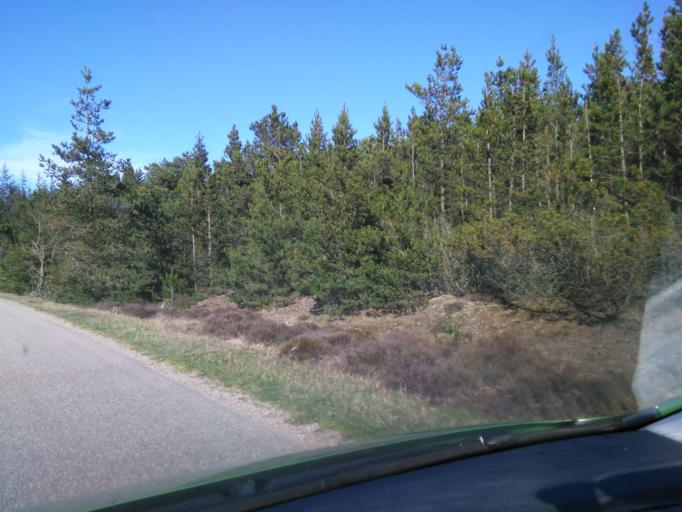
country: DK
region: South Denmark
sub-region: Varde Kommune
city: Oksbol
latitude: 55.7002
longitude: 8.2010
